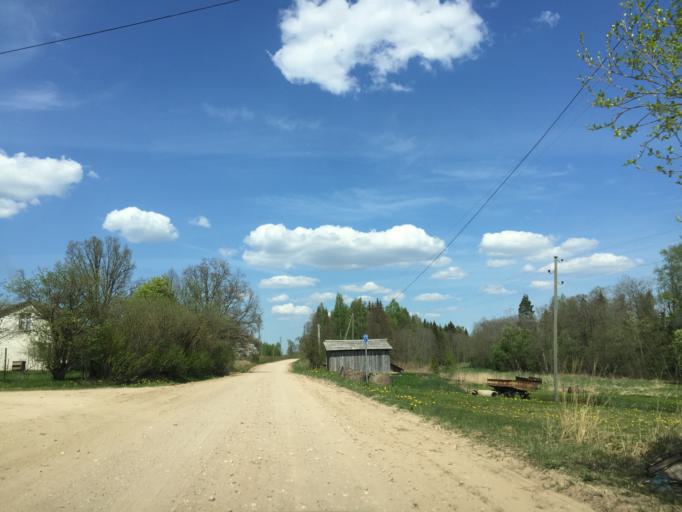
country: LV
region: Limbazu Rajons
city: Limbazi
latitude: 57.3643
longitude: 24.6373
